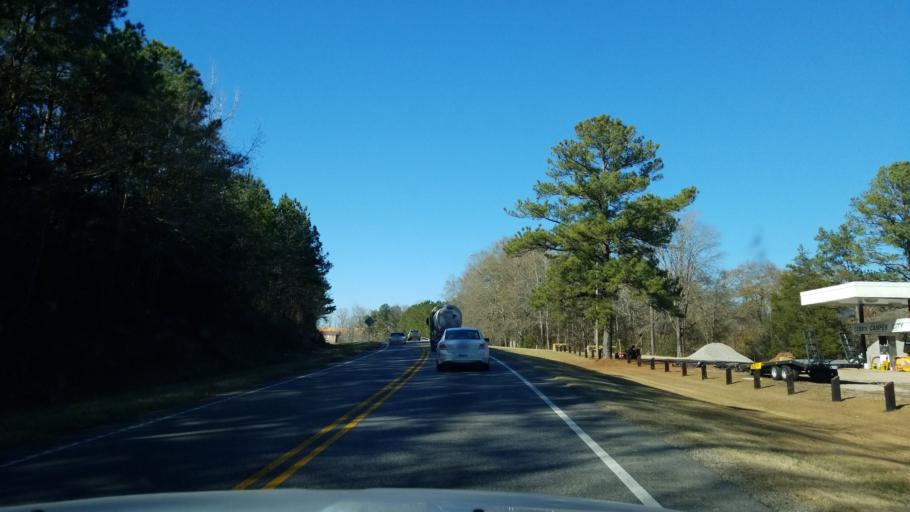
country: US
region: Alabama
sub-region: Pickens County
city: Gordo
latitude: 33.3297
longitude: -87.9125
